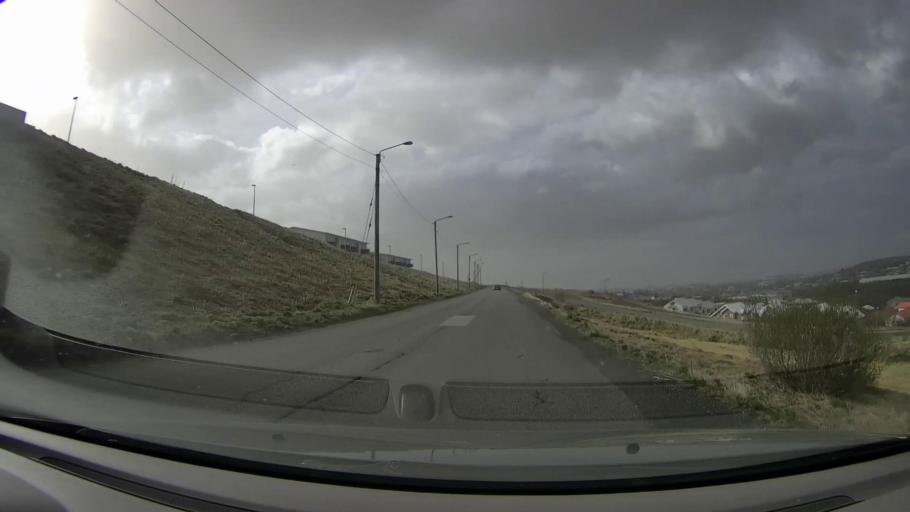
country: IS
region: Capital Region
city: Hafnarfjoerdur
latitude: 64.0571
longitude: -21.9325
